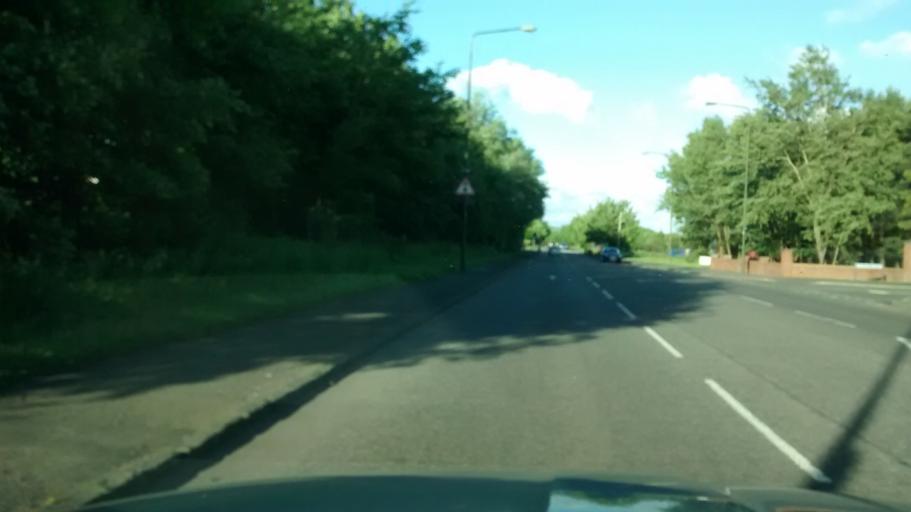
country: GB
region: Scotland
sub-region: West Lothian
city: Armadale
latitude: 55.8993
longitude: -3.6879
